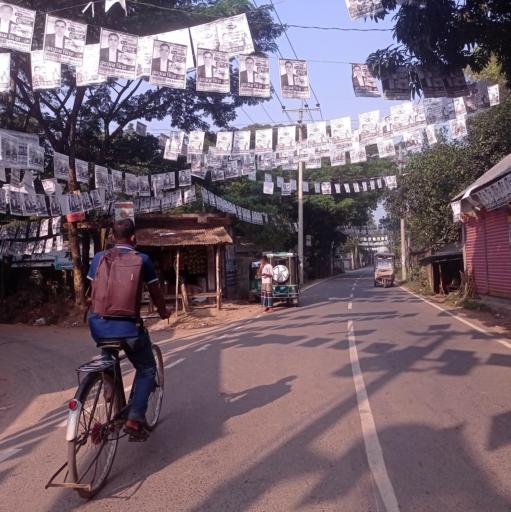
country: BD
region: Dhaka
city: Bhairab Bazar
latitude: 24.0391
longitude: 90.8322
